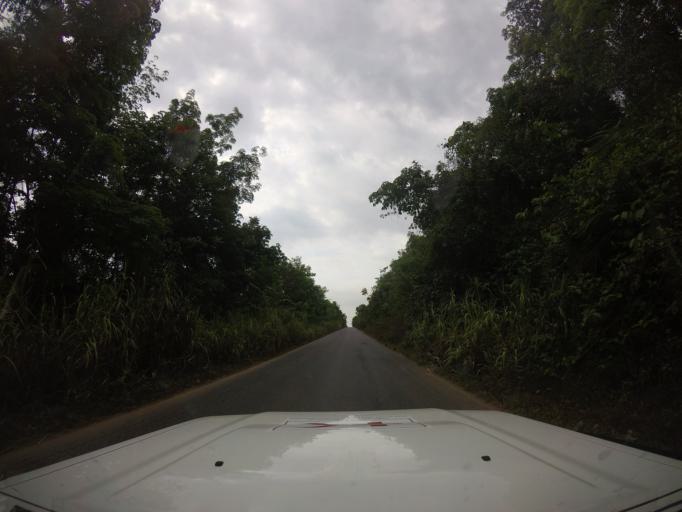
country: LR
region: Montserrado
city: Monrovia
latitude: 6.5420
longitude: -10.8576
